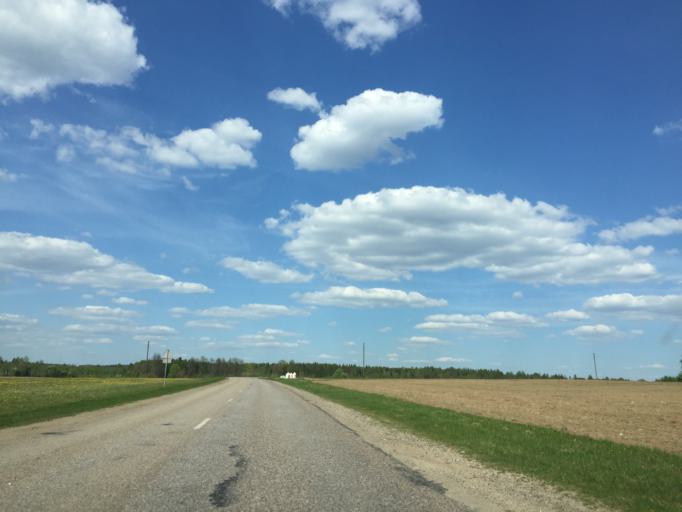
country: LV
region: Limbazu Rajons
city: Limbazi
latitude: 57.3842
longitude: 24.6868
